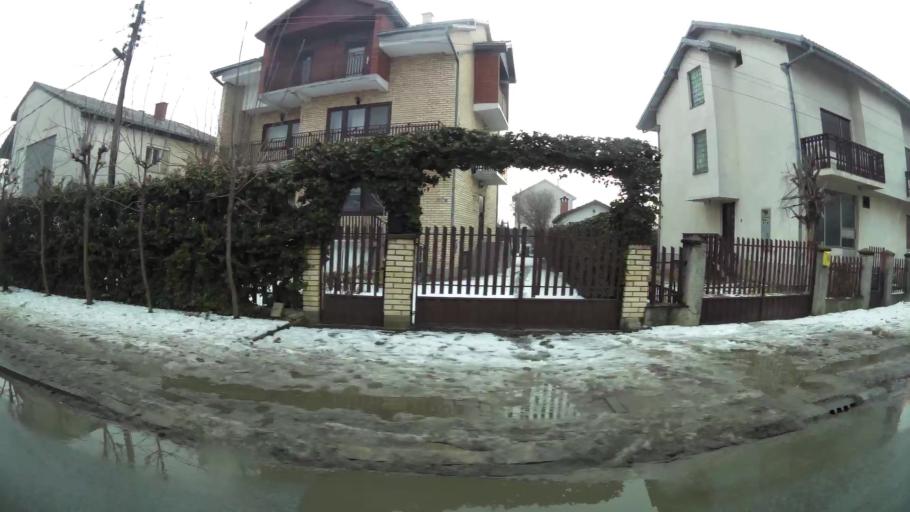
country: MK
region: Ilinden
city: Ilinden
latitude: 41.9963
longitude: 21.5807
